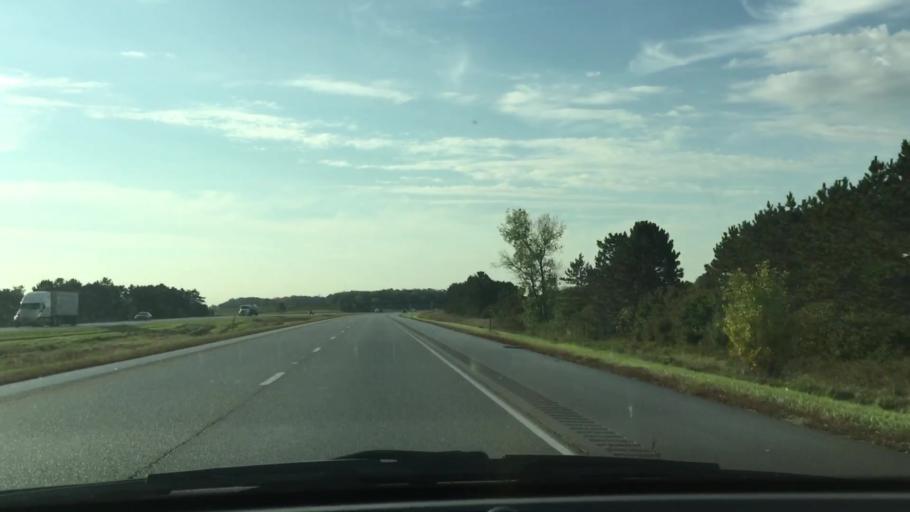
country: US
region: Illinois
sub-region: Ogle County
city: Davis Junction
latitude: 42.0632
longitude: -89.0213
